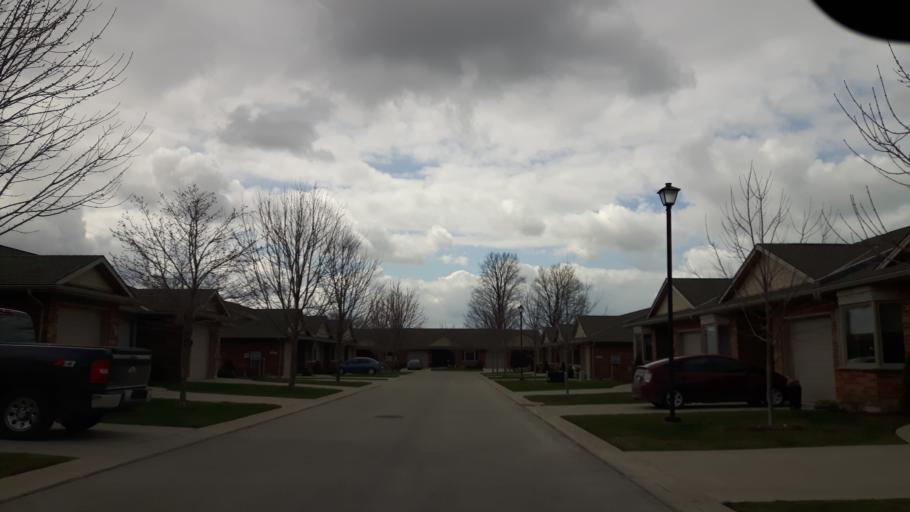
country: CA
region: Ontario
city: Bluewater
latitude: 43.5484
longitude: -81.6926
